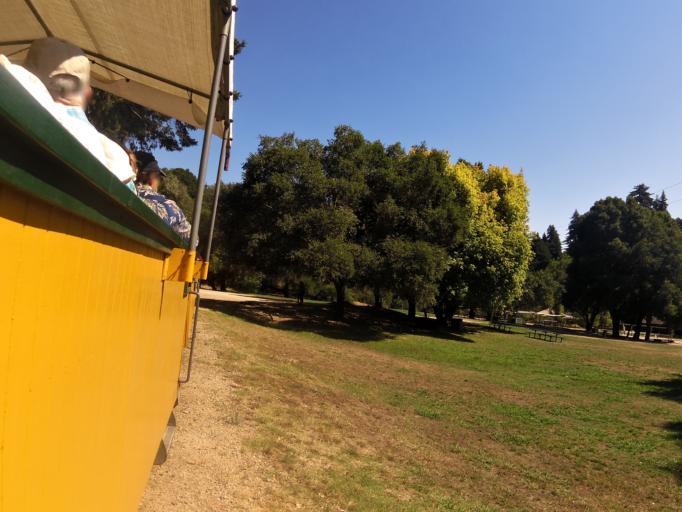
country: US
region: California
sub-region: Santa Cruz County
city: Mount Hermon
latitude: 37.0415
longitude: -122.0617
